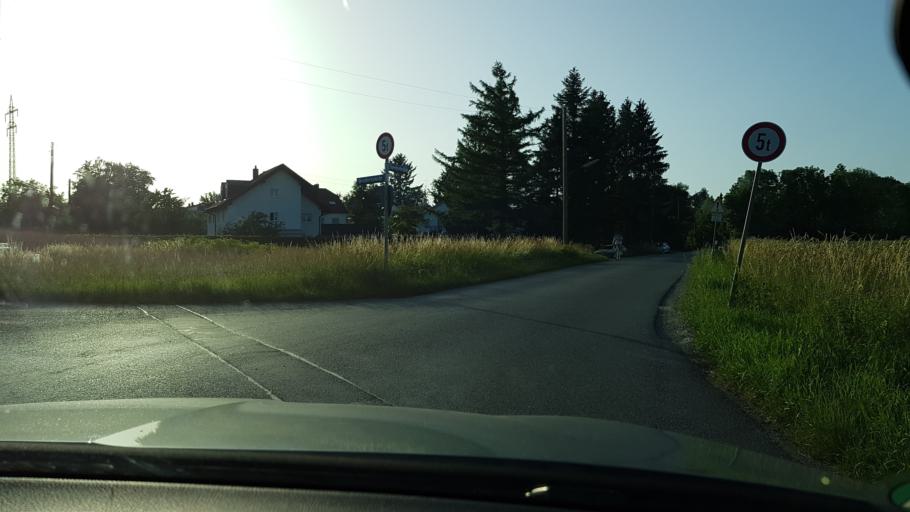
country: DE
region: Bavaria
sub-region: Upper Bavaria
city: Unterfoehring
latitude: 48.1542
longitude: 11.6566
